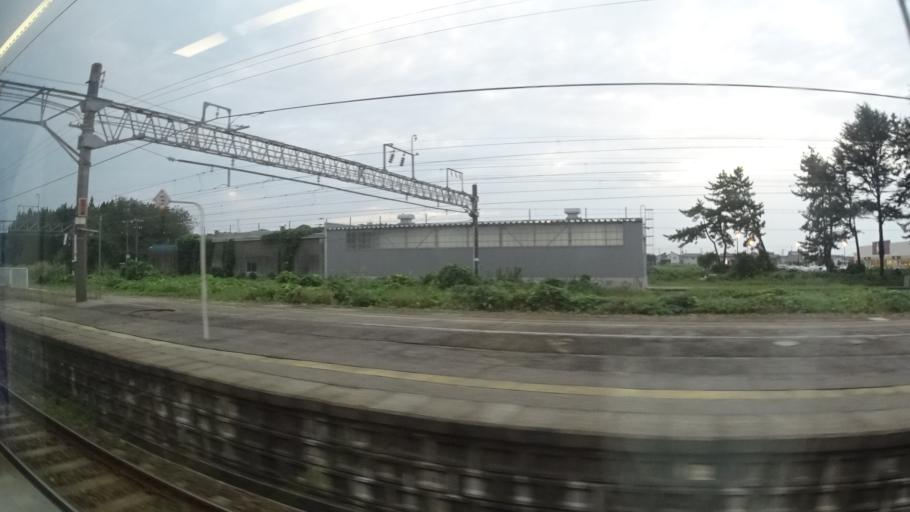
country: JP
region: Niigata
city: Murakami
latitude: 38.2194
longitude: 139.4633
